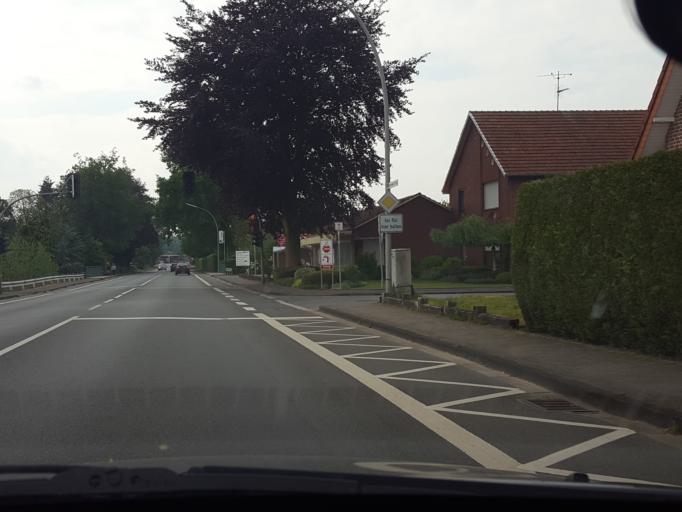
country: DE
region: North Rhine-Westphalia
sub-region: Regierungsbezirk Munster
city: Sudlohn
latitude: 51.9364
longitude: 6.8013
